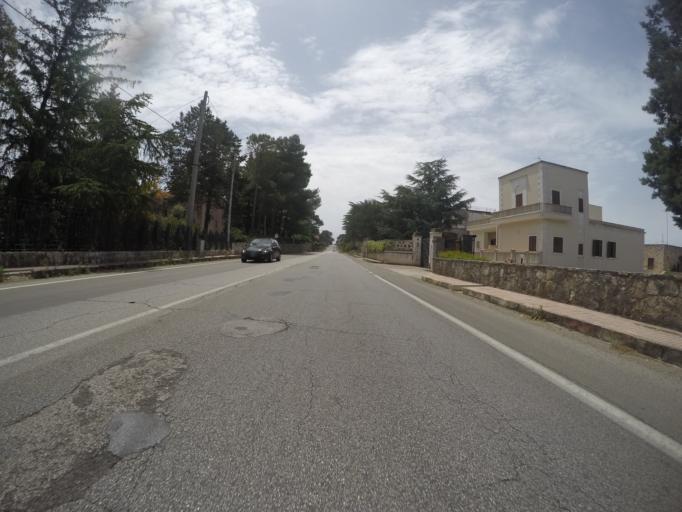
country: IT
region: Apulia
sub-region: Provincia di Taranto
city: Martina Franca
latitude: 40.6920
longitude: 17.3350
